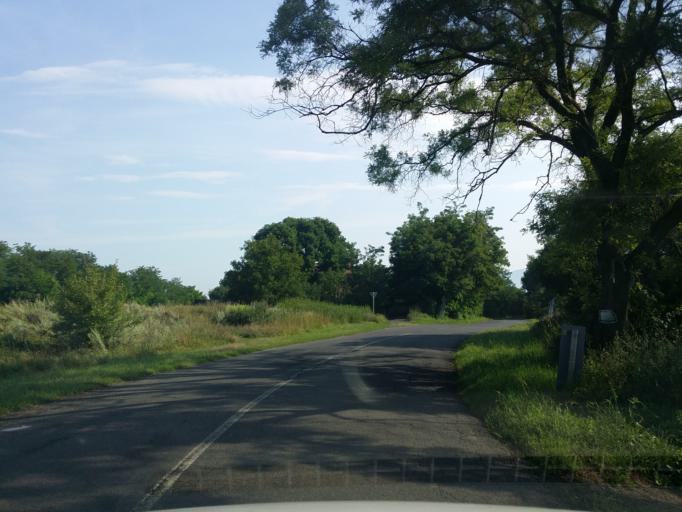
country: HU
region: Borsod-Abauj-Zemplen
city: Abaujszanto
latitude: 48.3635
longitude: 21.2187
